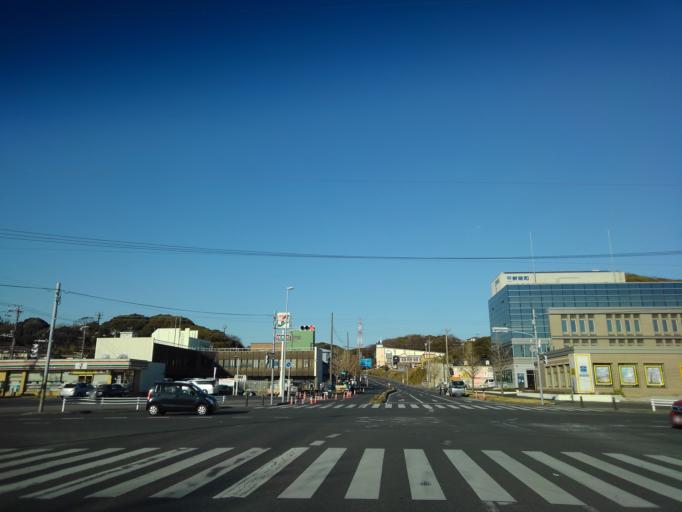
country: JP
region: Chiba
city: Kimitsu
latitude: 35.3372
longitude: 139.8908
